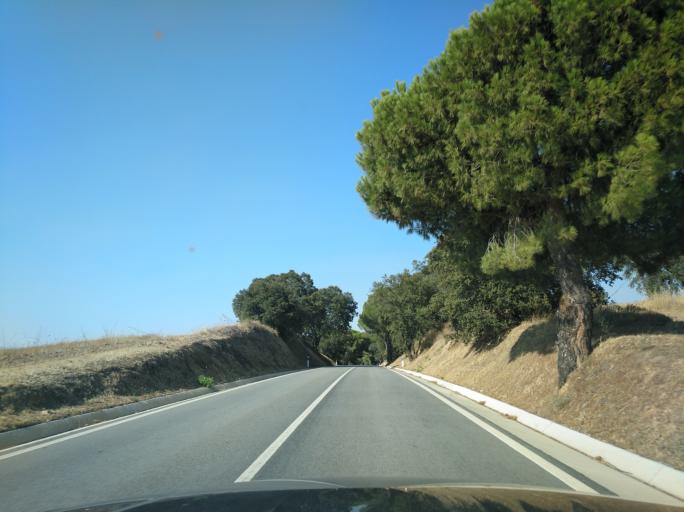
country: ES
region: Andalusia
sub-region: Provincia de Huelva
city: Rosal de la Frontera
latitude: 38.0345
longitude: -7.2679
